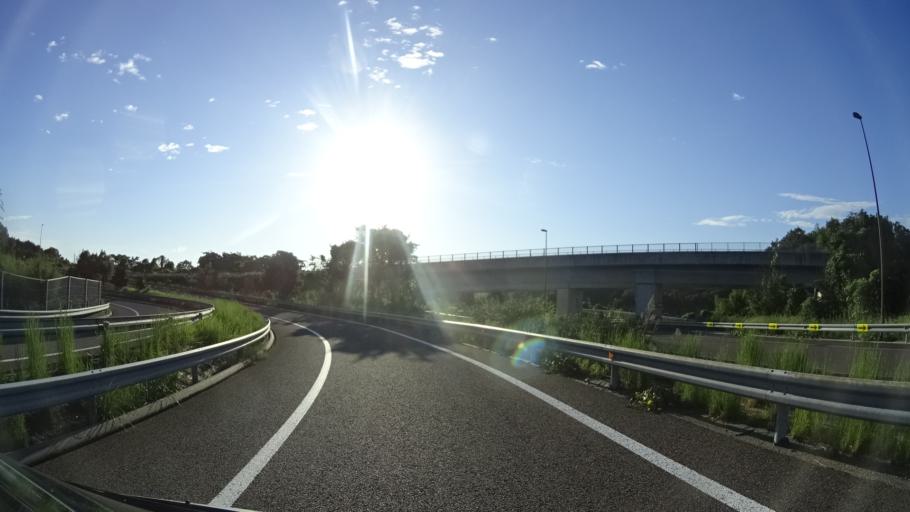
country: JP
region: Gifu
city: Minokamo
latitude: 35.4713
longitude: 137.0235
